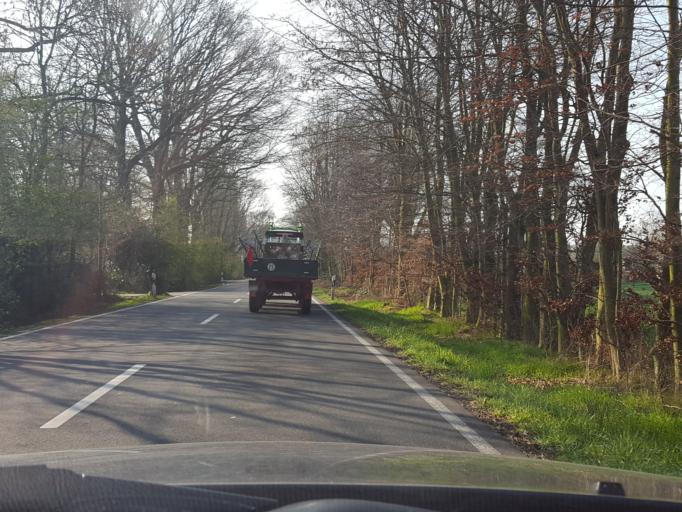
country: DE
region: North Rhine-Westphalia
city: Oer-Erkenschwick
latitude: 51.6353
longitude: 7.2421
